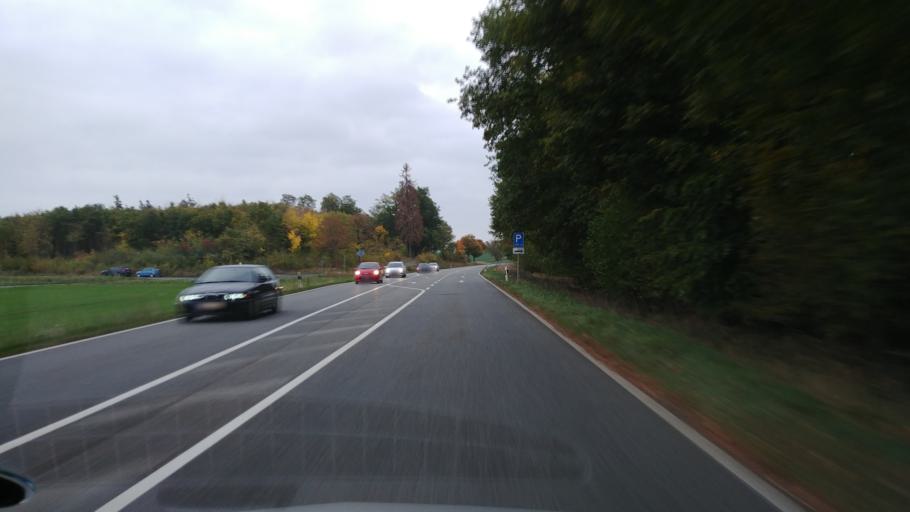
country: DE
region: Hesse
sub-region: Regierungsbezirk Darmstadt
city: Idstein
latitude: 50.2381
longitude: 8.1943
